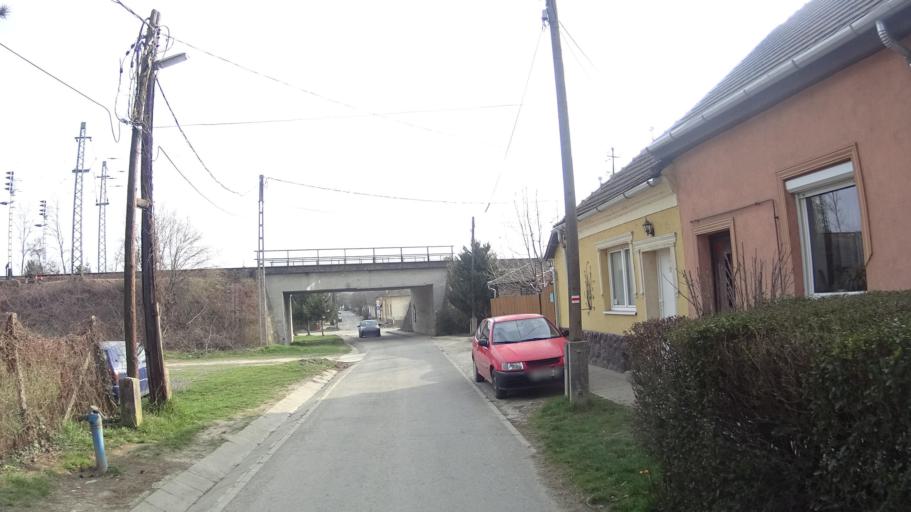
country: HU
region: Pest
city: Veroce
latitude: 47.8247
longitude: 19.0373
